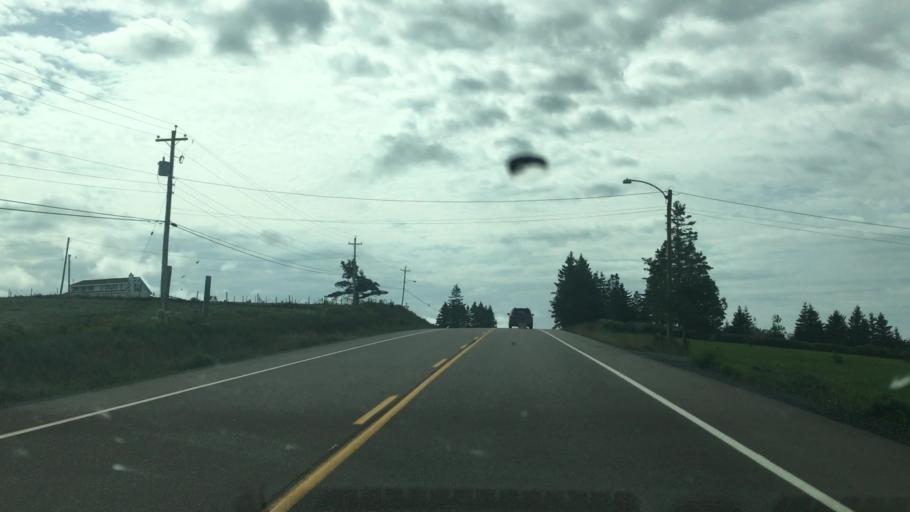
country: CA
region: Nova Scotia
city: Princeville
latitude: 45.6983
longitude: -60.7365
